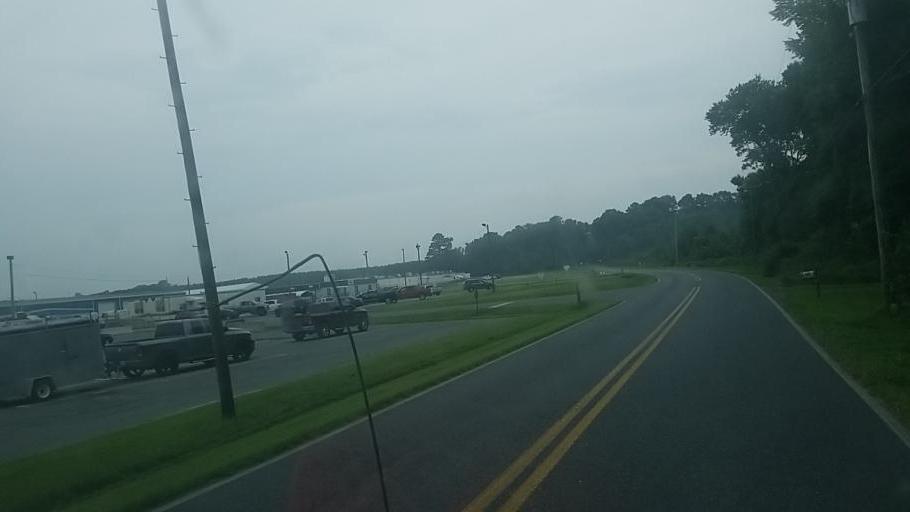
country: US
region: Maryland
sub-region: Wicomico County
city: Salisbury
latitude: 38.3836
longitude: -75.5266
